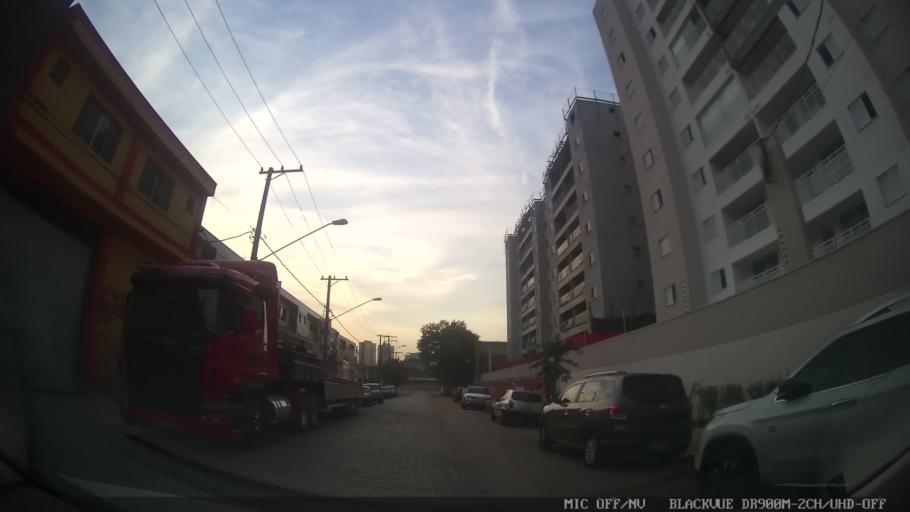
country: BR
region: Sao Paulo
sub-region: Sao Caetano Do Sul
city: Sao Caetano do Sul
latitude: -23.5982
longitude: -46.5938
